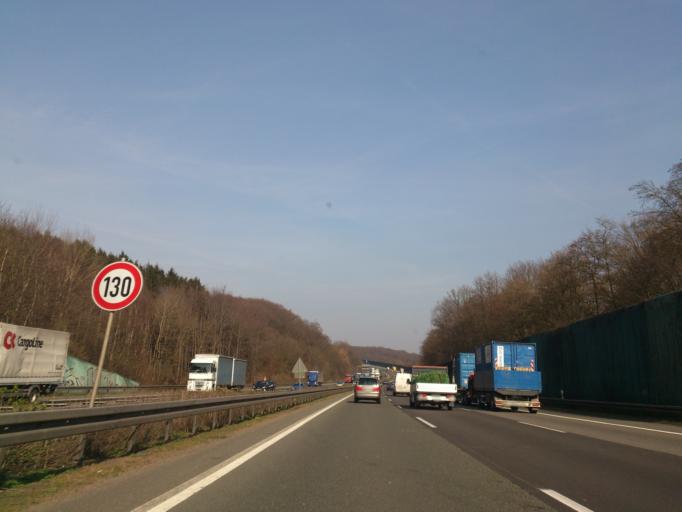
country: DE
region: North Rhine-Westphalia
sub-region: Regierungsbezirk Arnsberg
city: Schwelm
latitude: 51.3242
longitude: 7.2979
